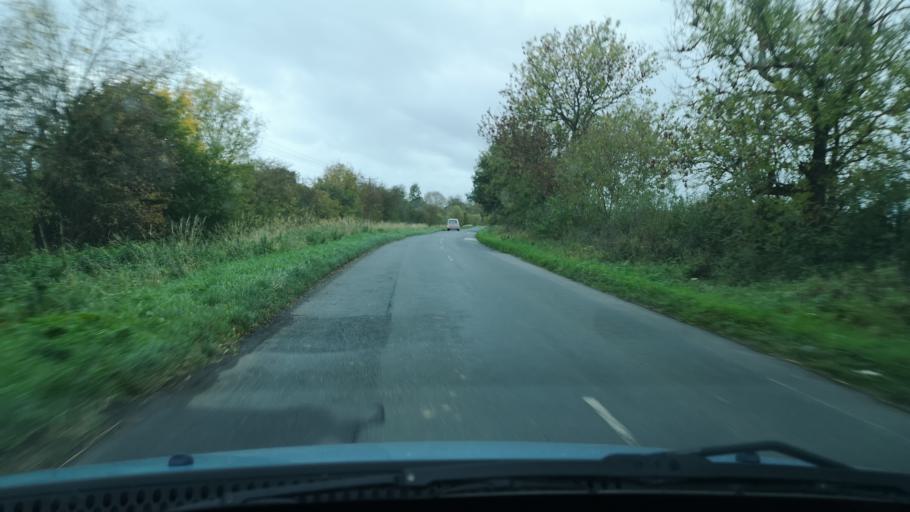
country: GB
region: England
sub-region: Doncaster
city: Hatfield
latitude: 53.6180
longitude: -0.9910
